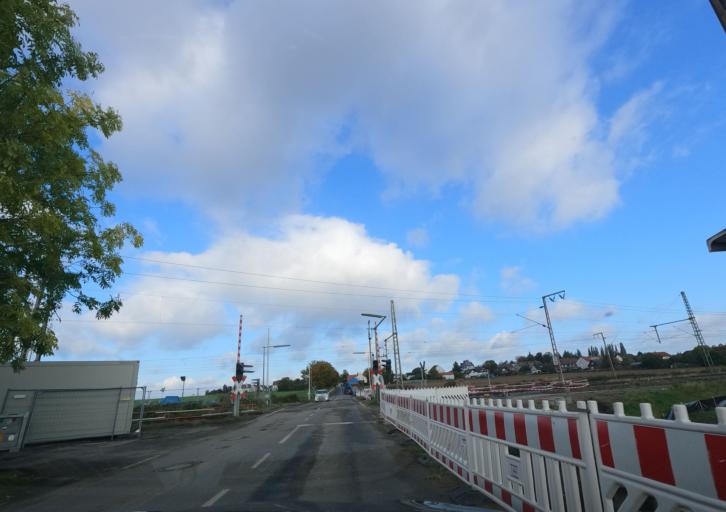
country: DE
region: Lower Saxony
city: Leiferde
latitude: 52.2340
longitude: 10.4515
